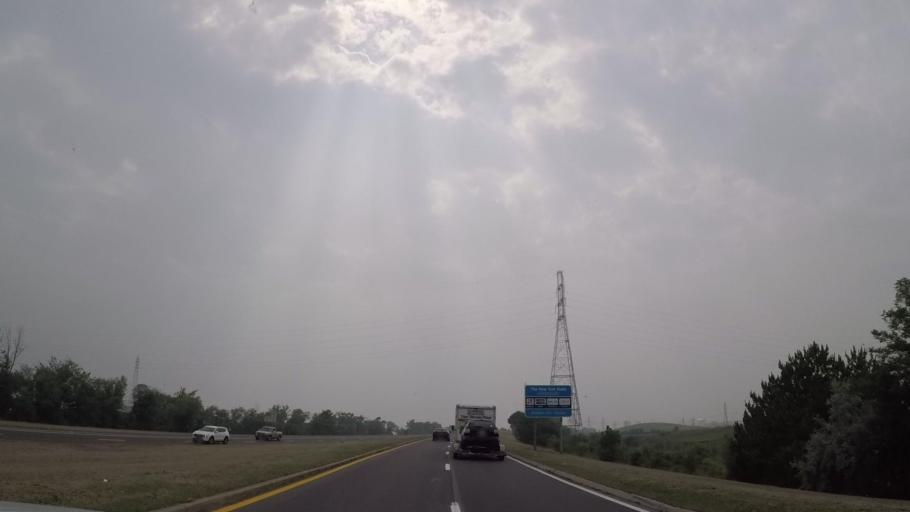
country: US
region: New York
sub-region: Niagara County
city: Niagara Falls
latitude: 43.0744
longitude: -78.9972
